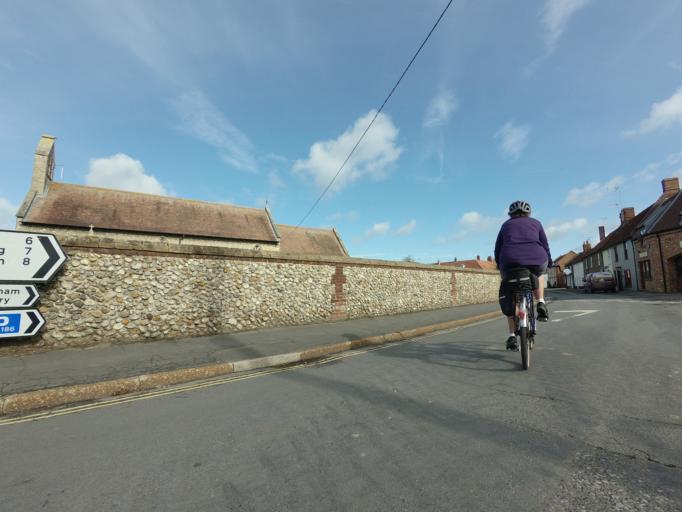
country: GB
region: England
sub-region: Norfolk
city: Wells-next-the-Sea
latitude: 52.9460
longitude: 0.7305
